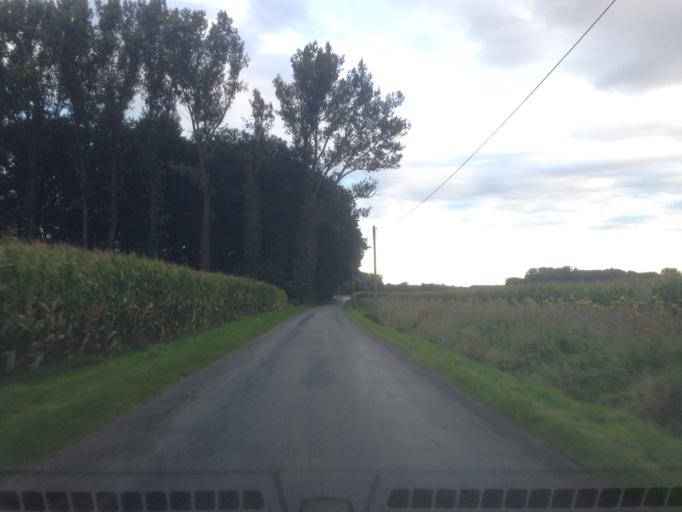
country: DE
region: North Rhine-Westphalia
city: Olfen
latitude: 51.7314
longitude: 7.3724
